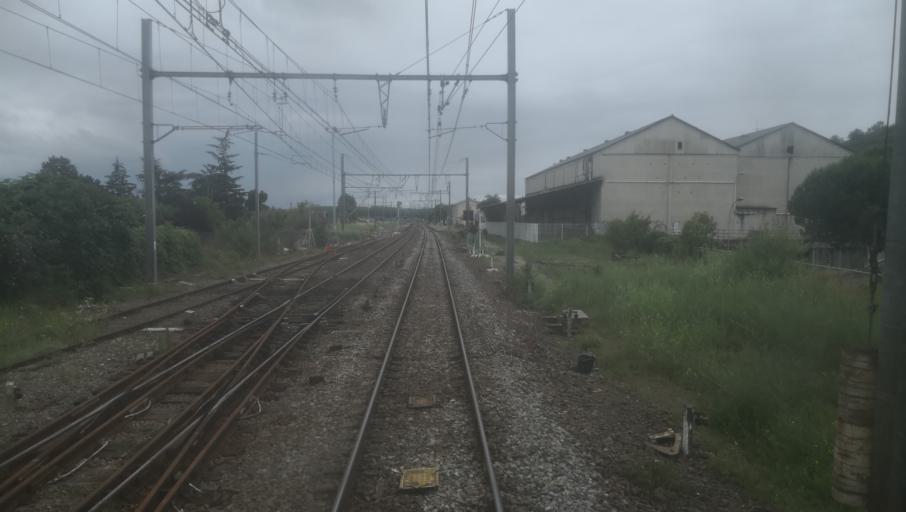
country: FR
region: Aquitaine
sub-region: Departement du Lot-et-Garonne
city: Port-Sainte-Marie
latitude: 44.2504
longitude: 0.3919
